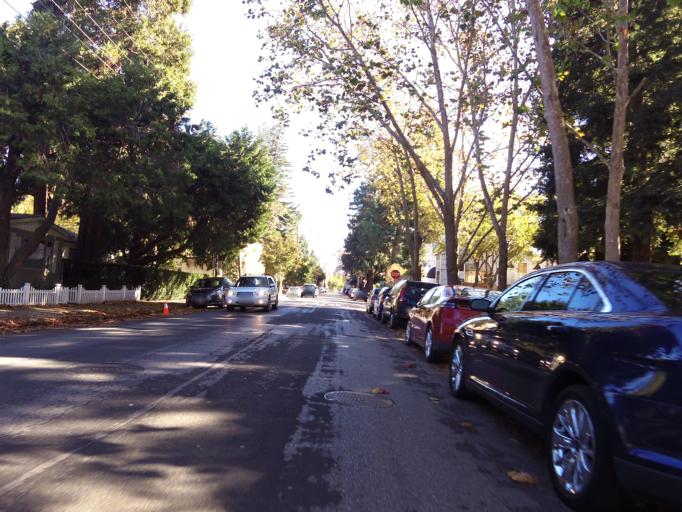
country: US
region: California
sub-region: Santa Clara County
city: Mountain View
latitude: 37.3895
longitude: -122.0851
